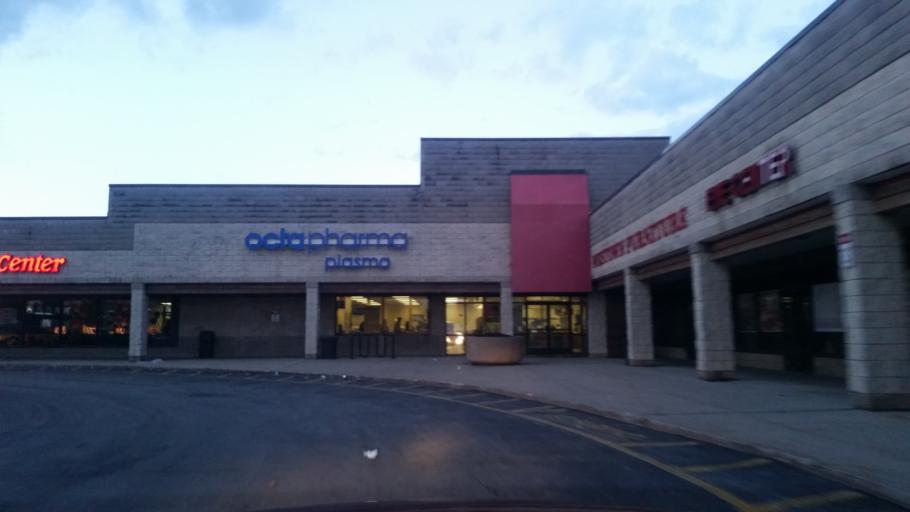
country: US
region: Ohio
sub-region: Cuyahoga County
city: Brooklyn
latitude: 41.4662
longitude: -81.7604
